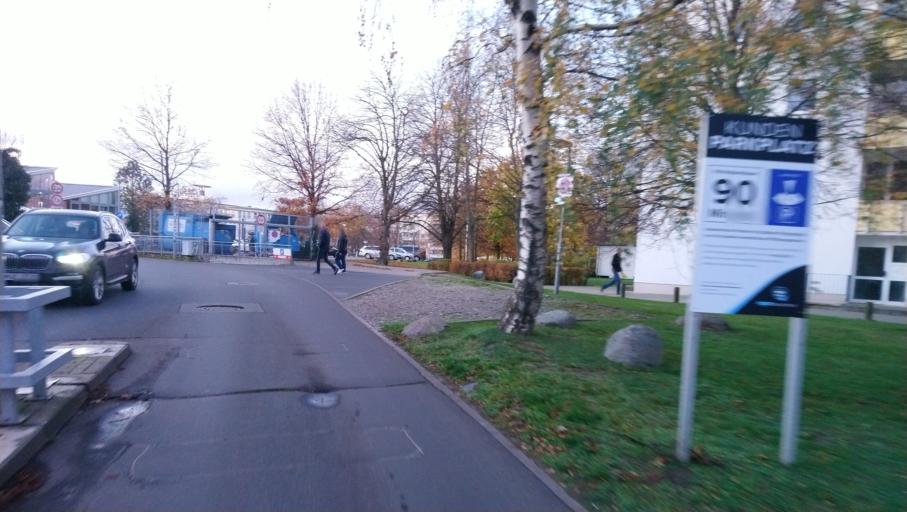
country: DE
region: Mecklenburg-Vorpommern
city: Rostock
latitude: 54.0712
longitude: 12.1188
